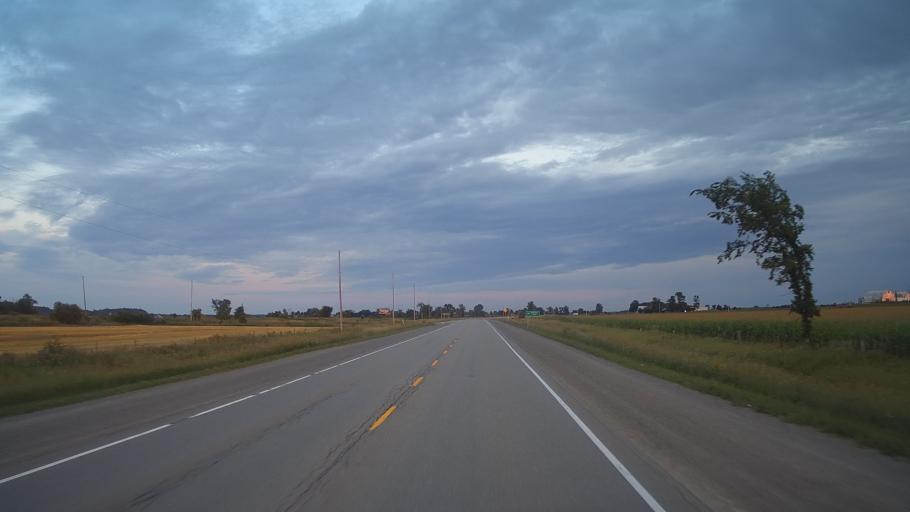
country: CA
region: Ontario
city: Pembroke
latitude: 45.6822
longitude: -76.9434
